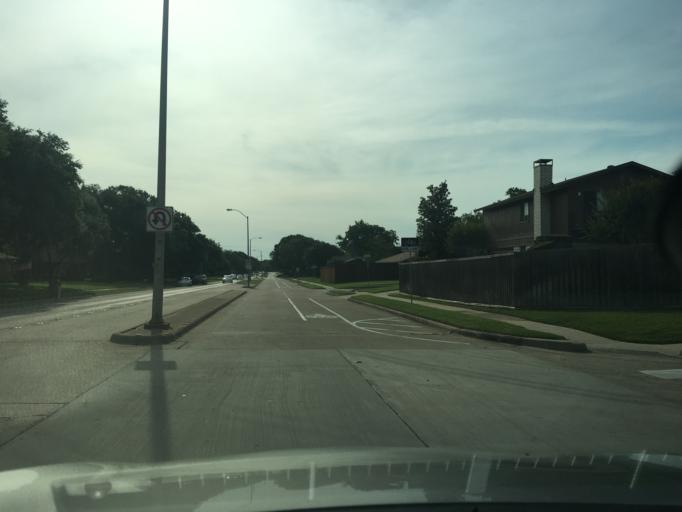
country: US
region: Texas
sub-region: Dallas County
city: Richardson
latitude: 32.9678
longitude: -96.6891
